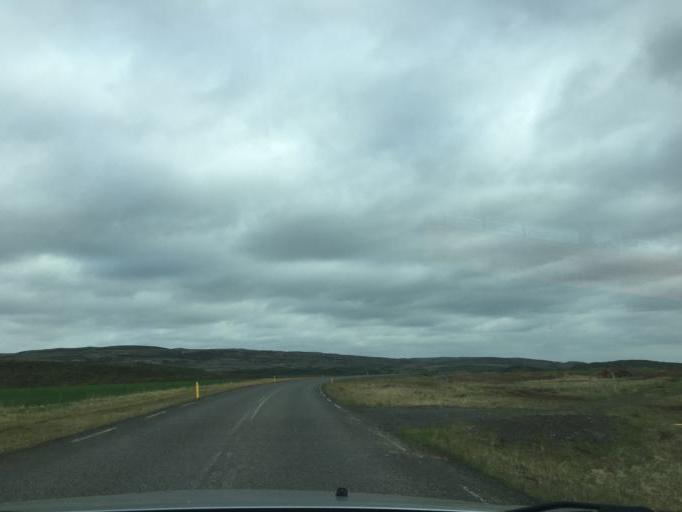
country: IS
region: South
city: Vestmannaeyjar
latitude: 64.2734
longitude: -20.2263
